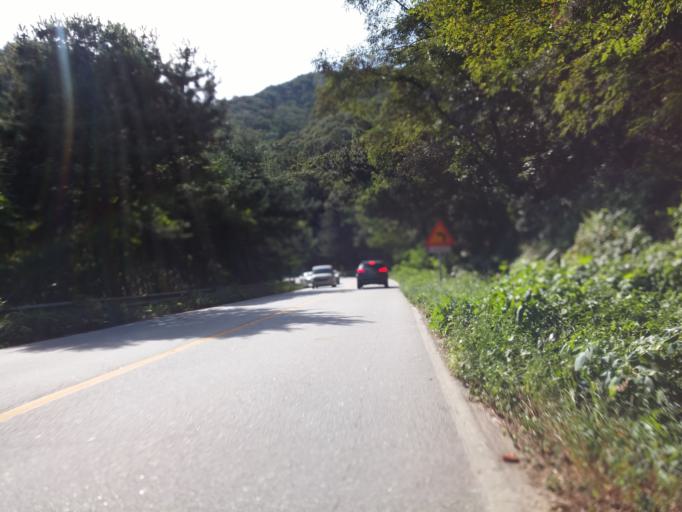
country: KR
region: Daejeon
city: Sintansin
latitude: 36.4815
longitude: 127.4849
